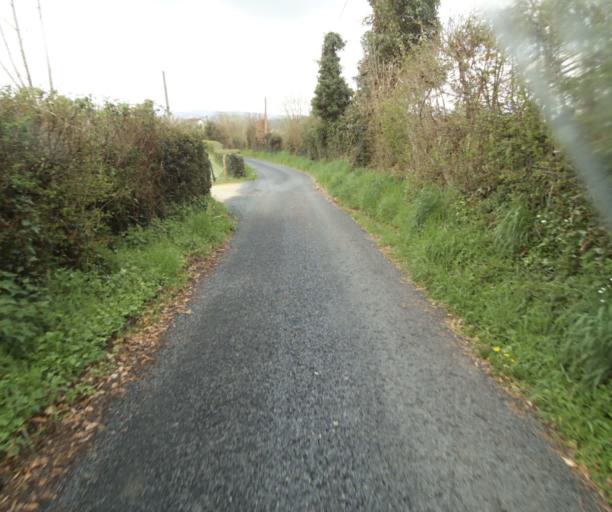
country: FR
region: Limousin
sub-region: Departement de la Correze
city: Tulle
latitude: 45.2800
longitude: 1.7967
